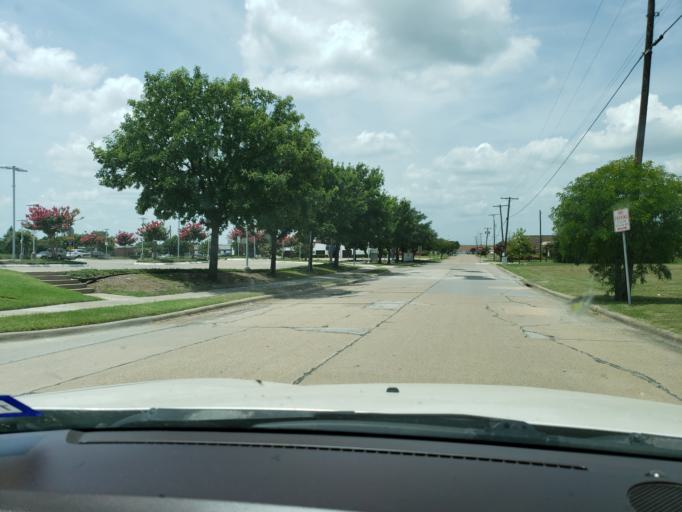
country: US
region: Texas
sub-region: Dallas County
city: Rowlett
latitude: 32.9063
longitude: -96.5624
